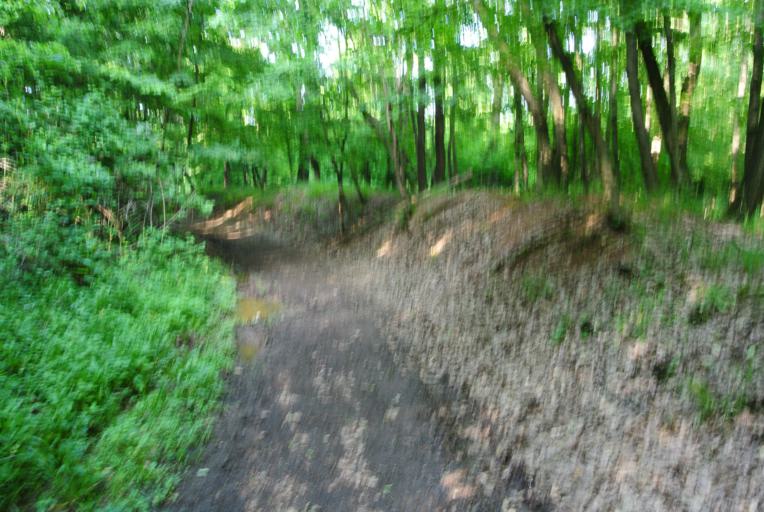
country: HU
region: Komarom-Esztergom
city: Tardos
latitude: 47.6570
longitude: 18.4776
